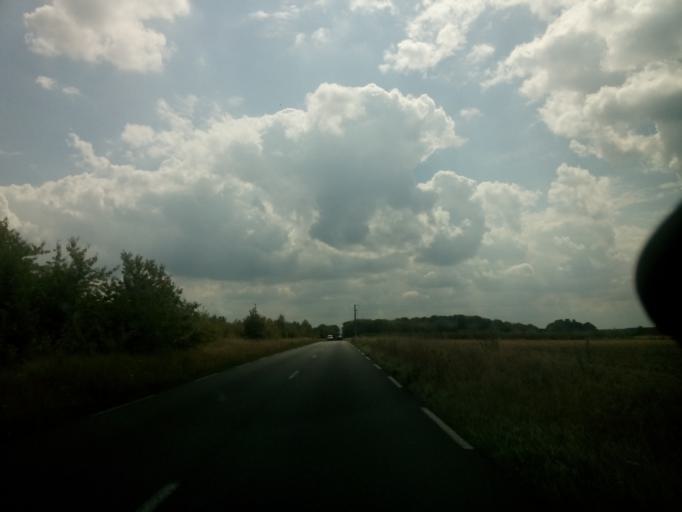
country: FR
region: Centre
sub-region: Departement d'Indre-et-Loire
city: Cheille
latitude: 47.2858
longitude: 0.4230
